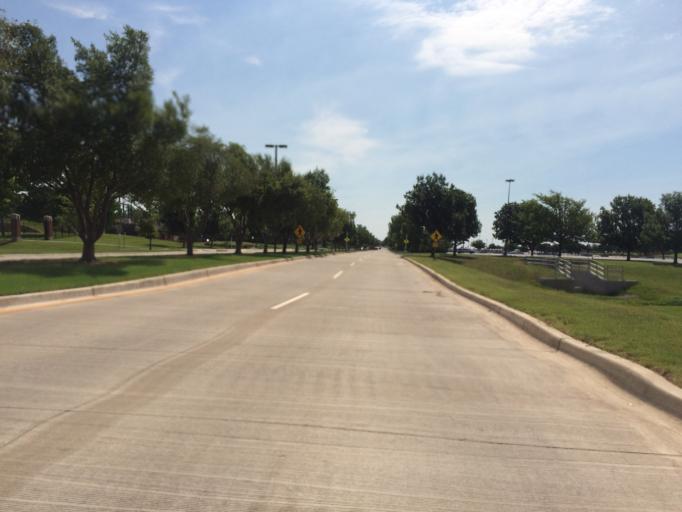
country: US
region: Oklahoma
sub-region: Cleveland County
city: Norman
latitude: 35.1894
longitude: -97.4481
